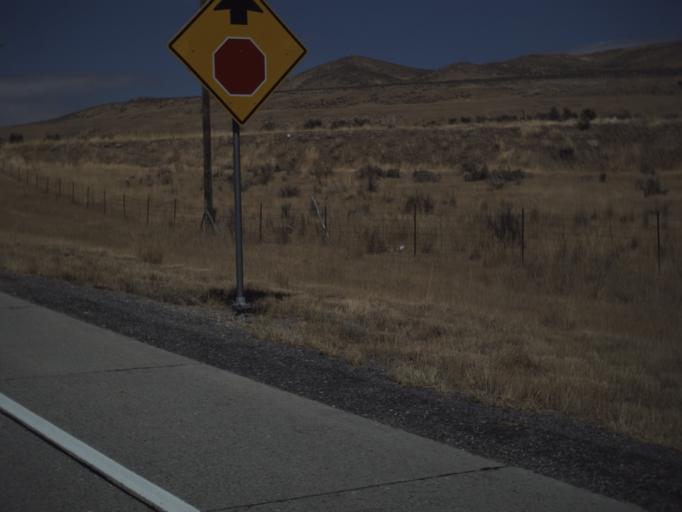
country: US
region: Utah
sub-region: Box Elder County
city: Tremonton
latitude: 41.7198
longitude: -112.2255
